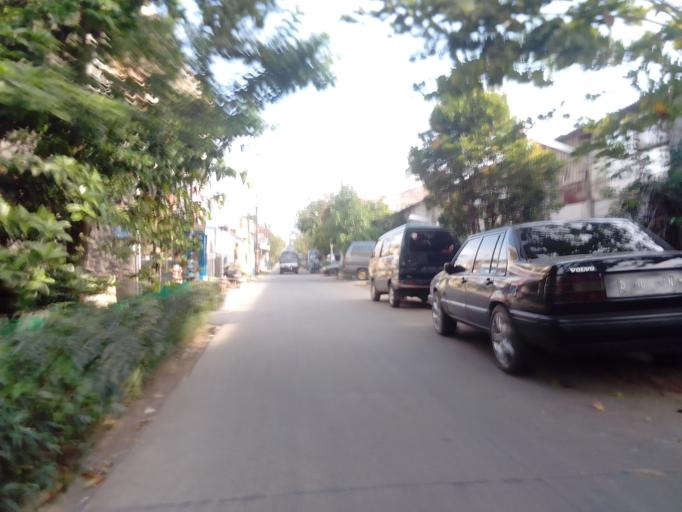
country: ID
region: West Java
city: Cileunyi
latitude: -6.9271
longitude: 107.7050
